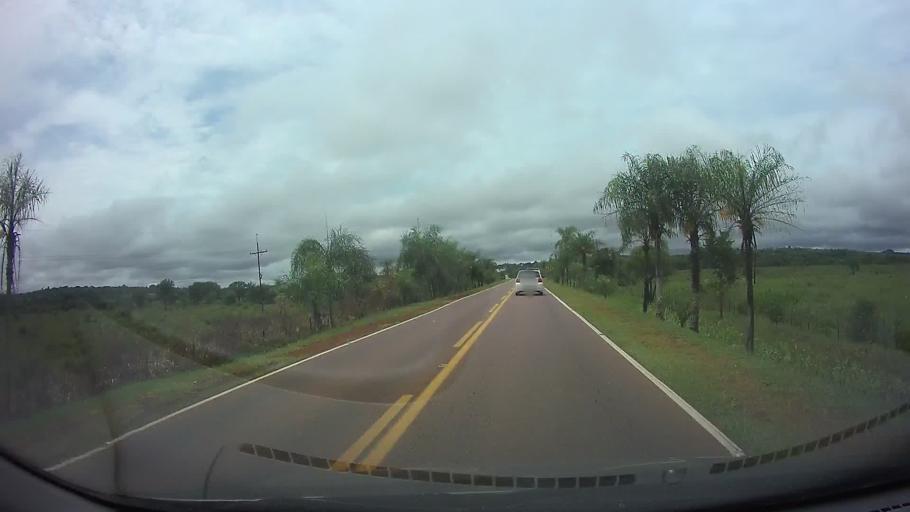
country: PY
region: Paraguari
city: Acahay
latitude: -25.8908
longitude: -57.1197
